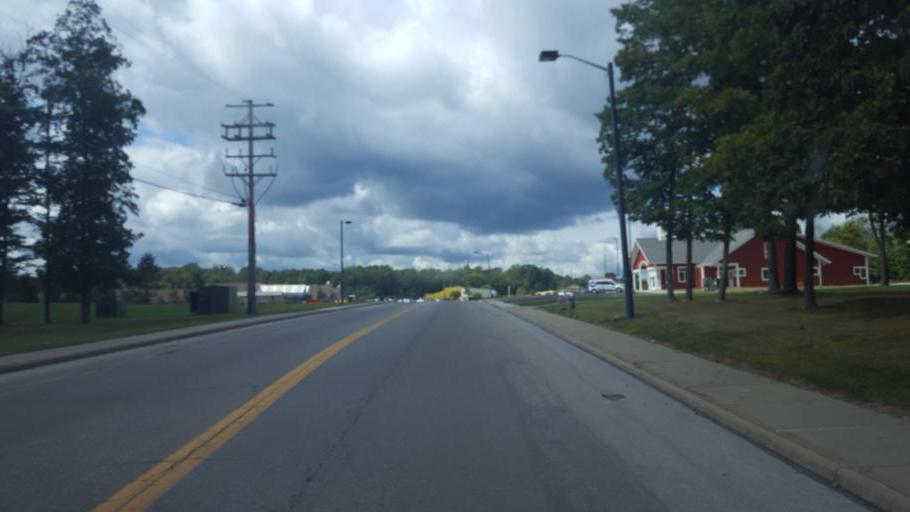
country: US
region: Ohio
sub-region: Geauga County
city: Middlefield
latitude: 41.4595
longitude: -81.0813
